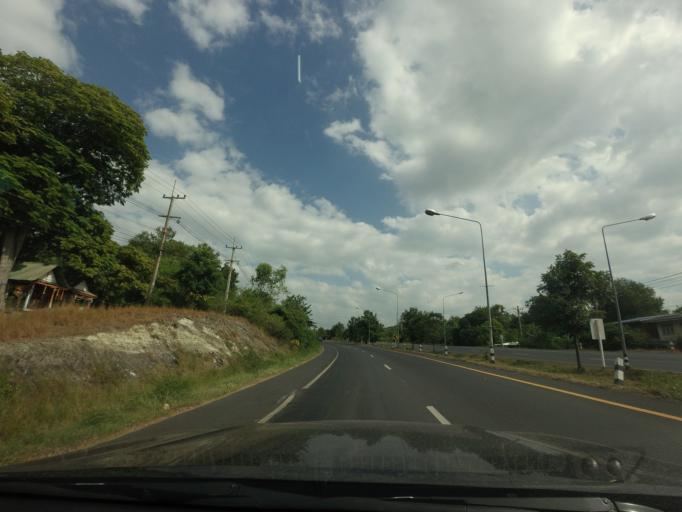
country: TH
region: Lop Buri
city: Chai Badan
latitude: 15.3022
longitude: 101.1248
